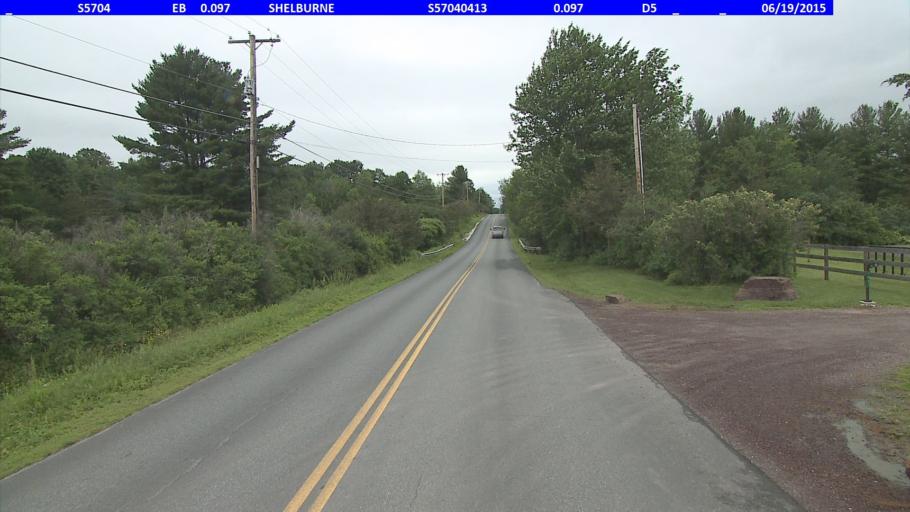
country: US
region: Vermont
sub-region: Chittenden County
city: Burlington
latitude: 44.3961
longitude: -73.2450
